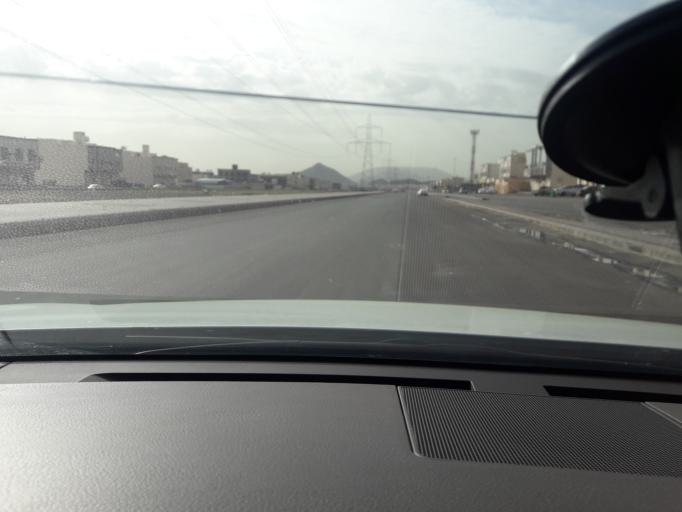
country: SA
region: Al Madinah al Munawwarah
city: Sultanah
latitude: 24.4343
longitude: 39.4930
